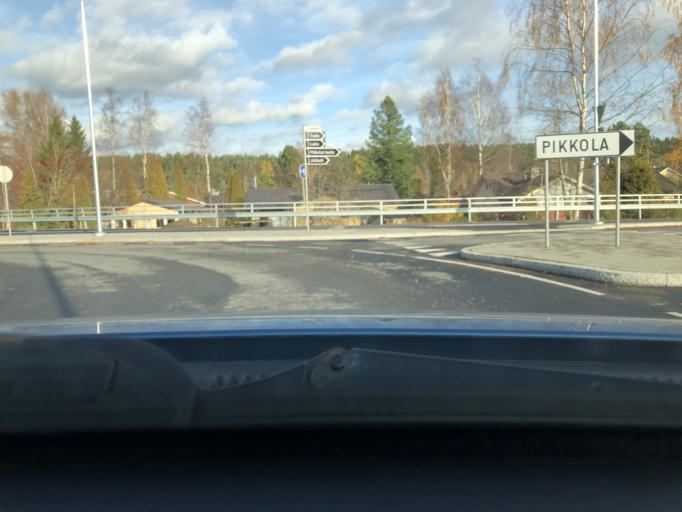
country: FI
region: Pirkanmaa
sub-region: Tampere
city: Kangasala
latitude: 61.4652
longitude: 24.0380
